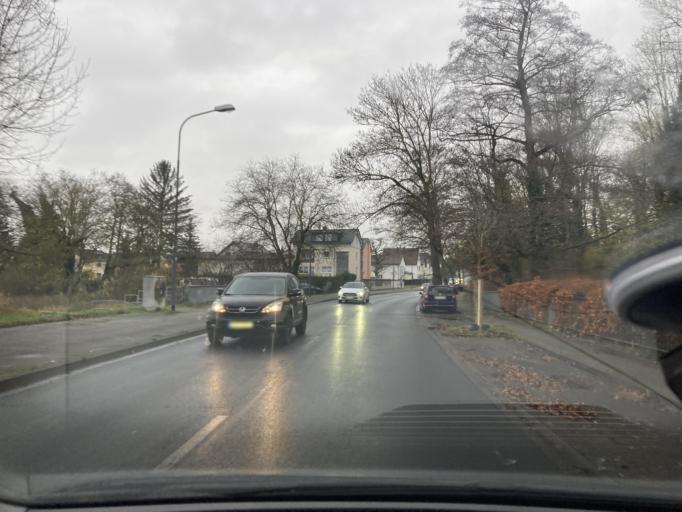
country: DE
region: Hesse
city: Heusenstamm
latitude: 50.0843
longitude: 8.8064
